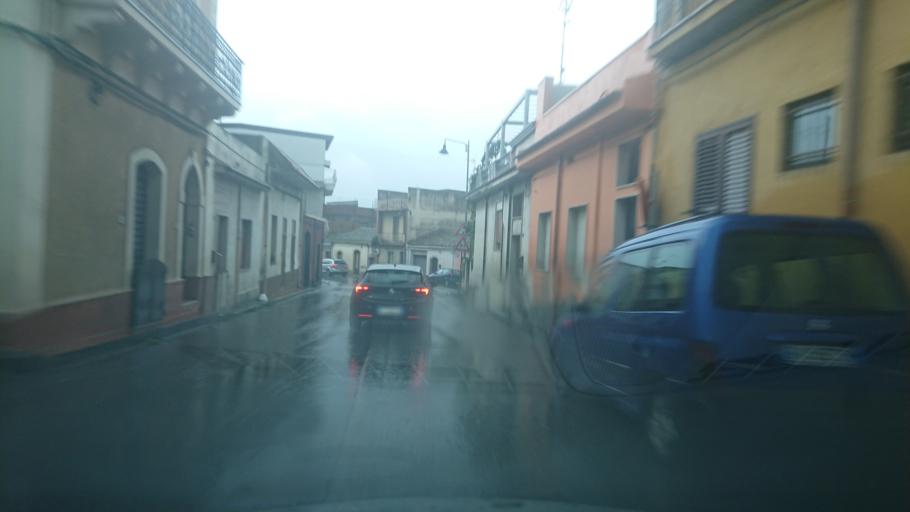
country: IT
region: Sicily
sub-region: Catania
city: Pasteria-Lapide
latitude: 37.8060
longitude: 15.2227
